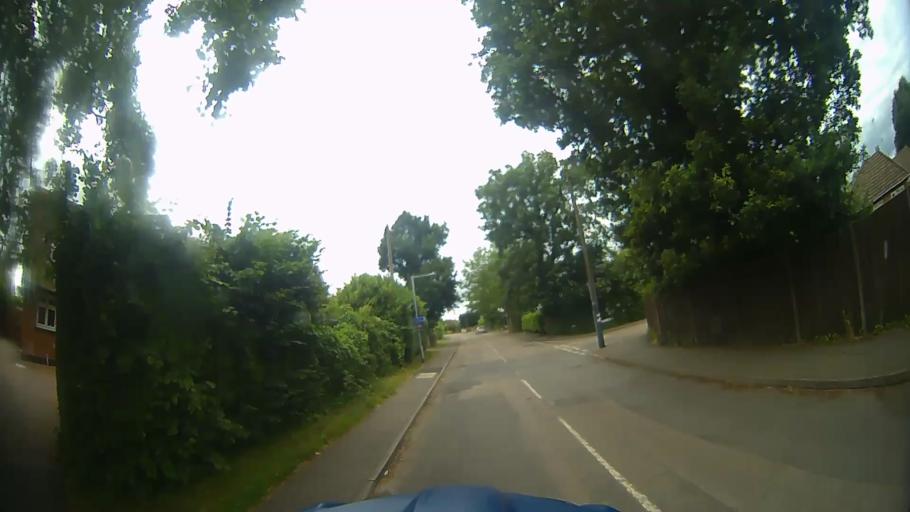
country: GB
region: England
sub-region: Wokingham
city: Winnersh
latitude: 51.4310
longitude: -0.8701
